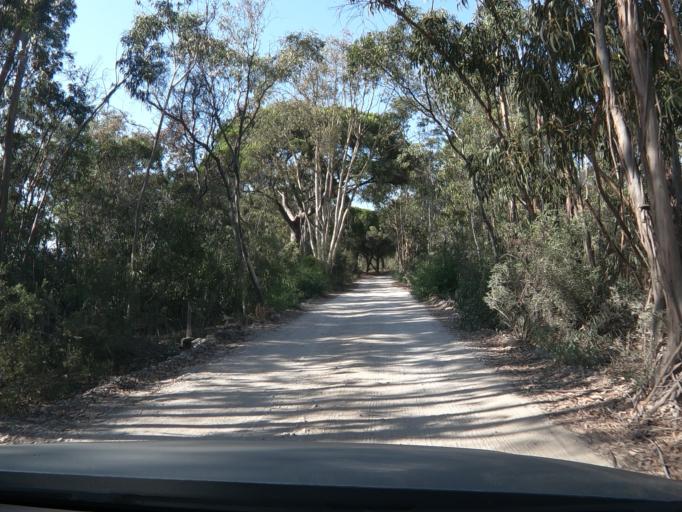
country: PT
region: Setubal
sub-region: Setubal
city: Setubal
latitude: 38.4755
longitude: -8.8793
